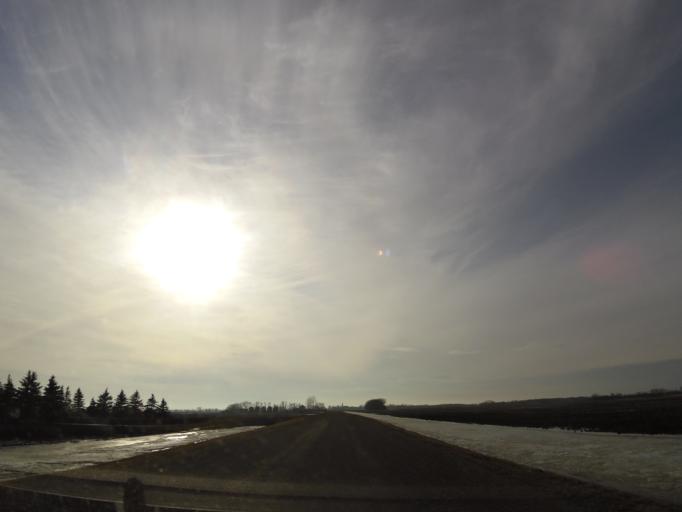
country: US
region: North Dakota
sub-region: Walsh County
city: Grafton
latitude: 48.4267
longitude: -97.2674
